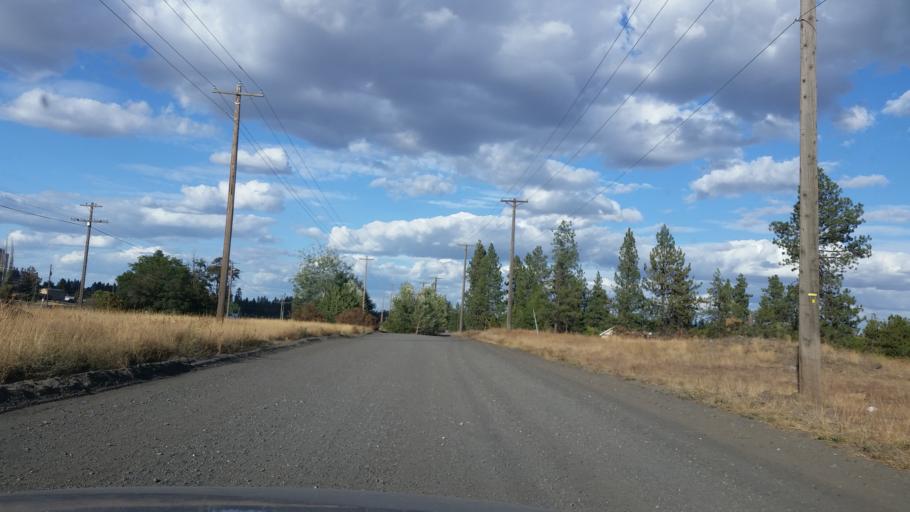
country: US
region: Washington
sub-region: Spokane County
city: Cheney
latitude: 47.4832
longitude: -117.5759
